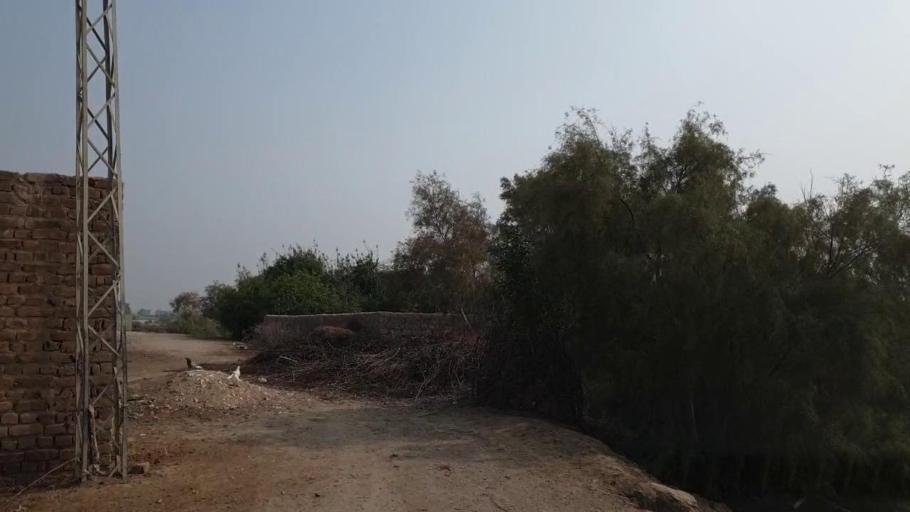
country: PK
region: Sindh
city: Bhan
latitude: 26.5072
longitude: 67.6742
